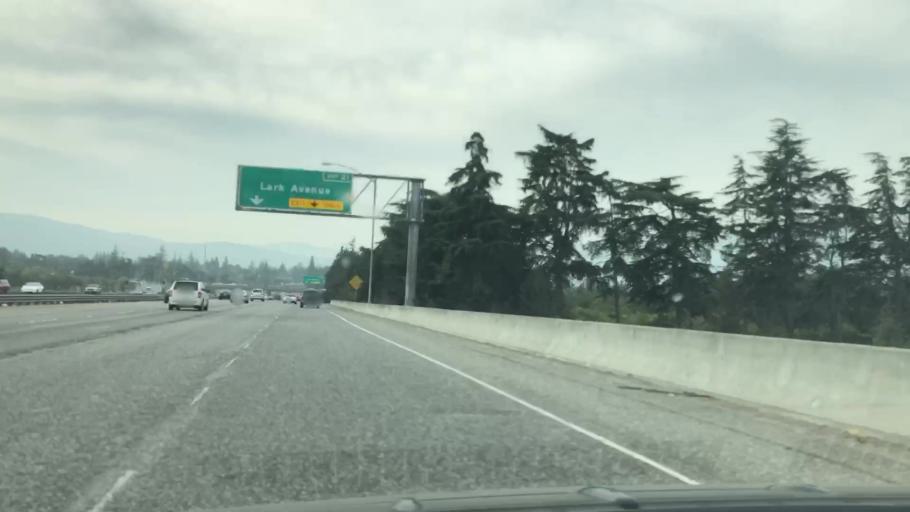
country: US
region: California
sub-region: Santa Clara County
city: Cambrian Park
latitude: 37.2537
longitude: -121.9575
